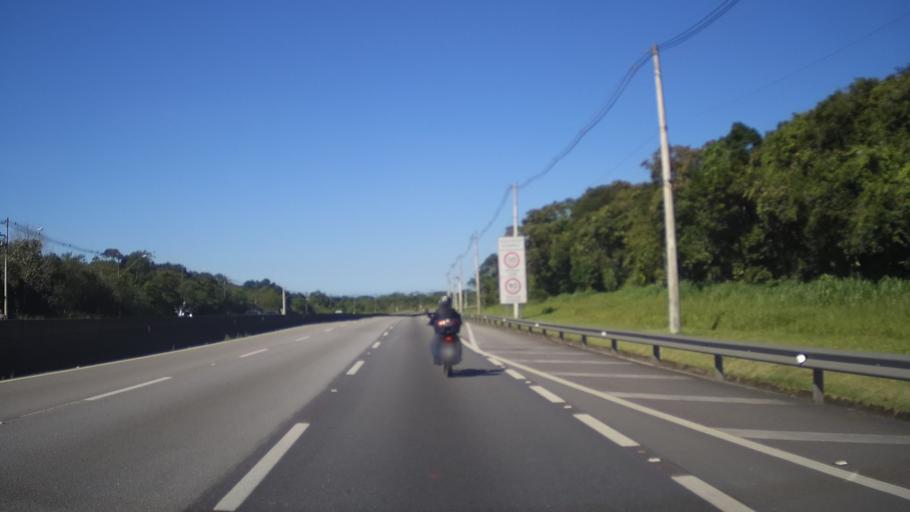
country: BR
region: Sao Paulo
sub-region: Sao Vicente
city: Sao Vicente
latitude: -23.9652
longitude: -46.4714
